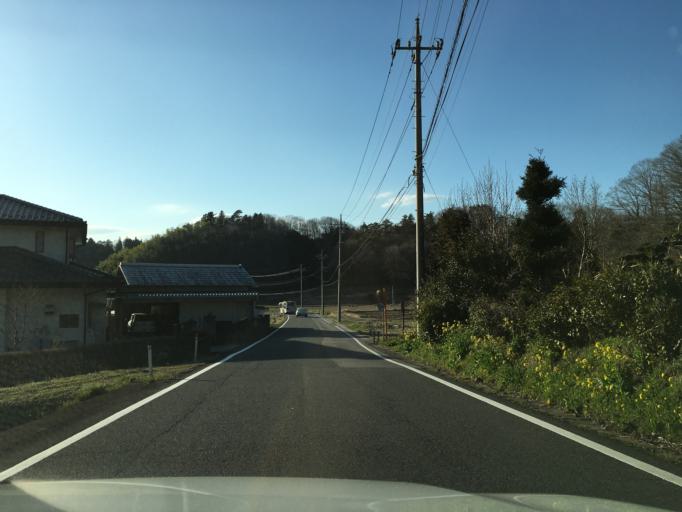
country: JP
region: Ibaraki
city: Daigo
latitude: 36.7746
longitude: 140.2484
